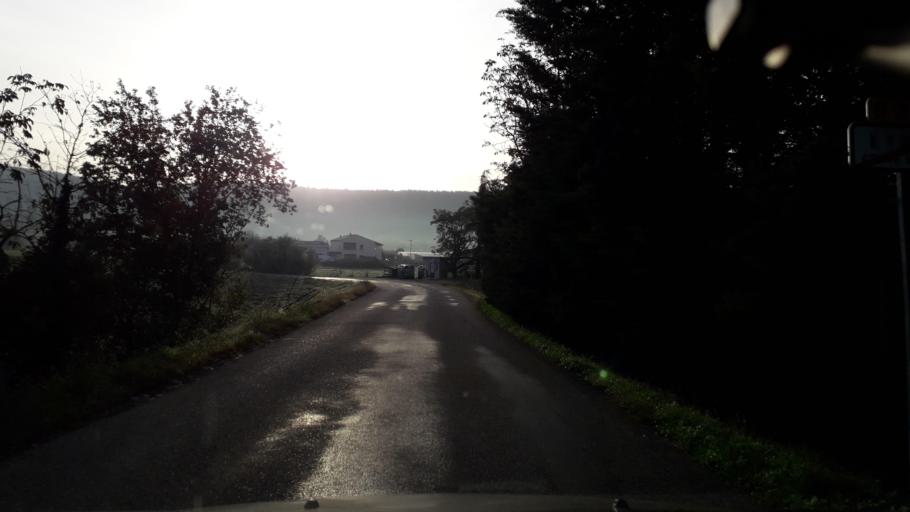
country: FR
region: Rhone-Alpes
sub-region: Departement de l'Ardeche
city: Lavilledieu
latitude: 44.6121
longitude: 4.4617
